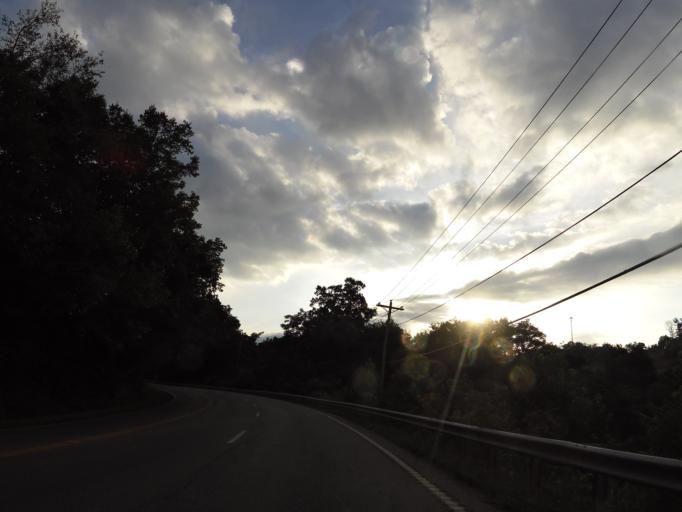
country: US
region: Tennessee
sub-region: Cocke County
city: Newport
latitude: 35.9559
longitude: -83.1476
